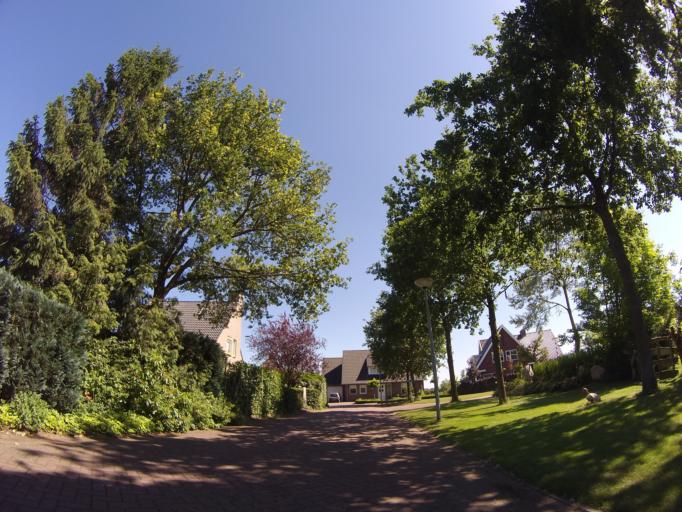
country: NL
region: Drenthe
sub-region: Gemeente Coevorden
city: Sleen
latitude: 52.7878
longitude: 6.8051
